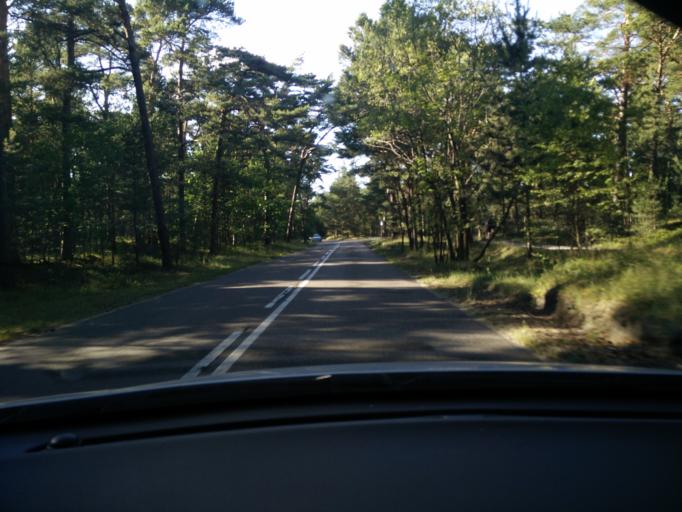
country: PL
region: Pomeranian Voivodeship
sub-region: Powiat pucki
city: Jastarnia
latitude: 54.6641
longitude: 18.7459
